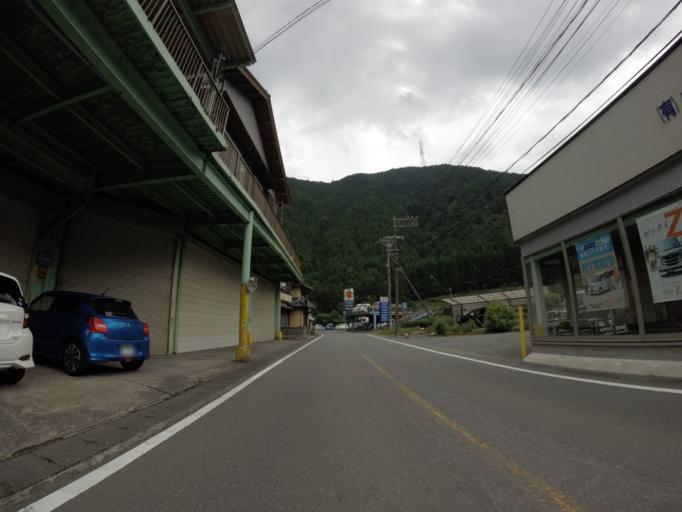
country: JP
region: Shizuoka
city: Fujinomiya
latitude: 35.1017
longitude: 138.4953
